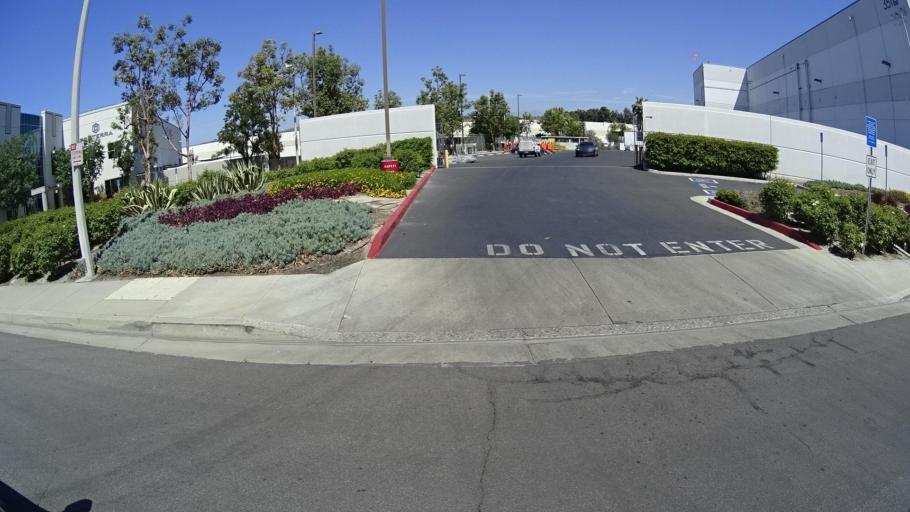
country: US
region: California
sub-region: Los Angeles County
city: Walnut
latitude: 34.0153
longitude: -117.8462
